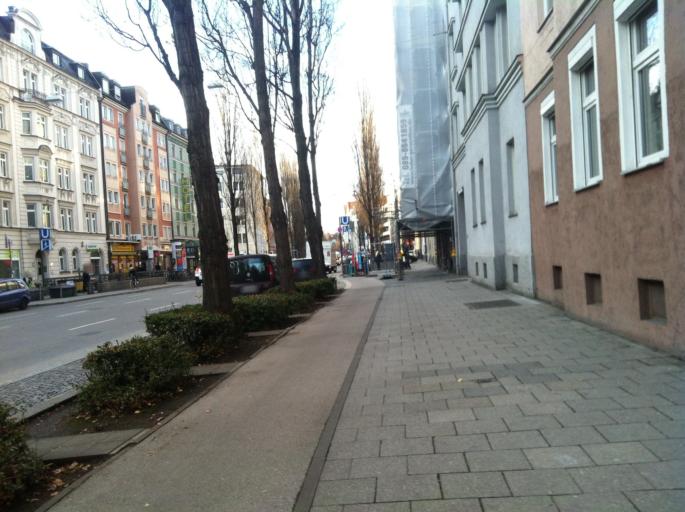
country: DE
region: Bavaria
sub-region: Upper Bavaria
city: Munich
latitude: 48.1264
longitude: 11.5523
